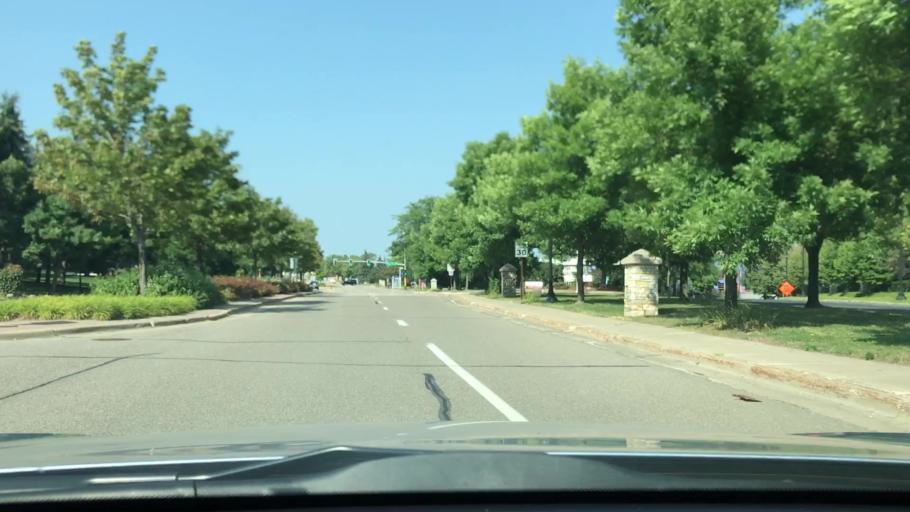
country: US
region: Minnesota
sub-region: Hennepin County
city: Edina
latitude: 44.9077
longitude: -93.3573
